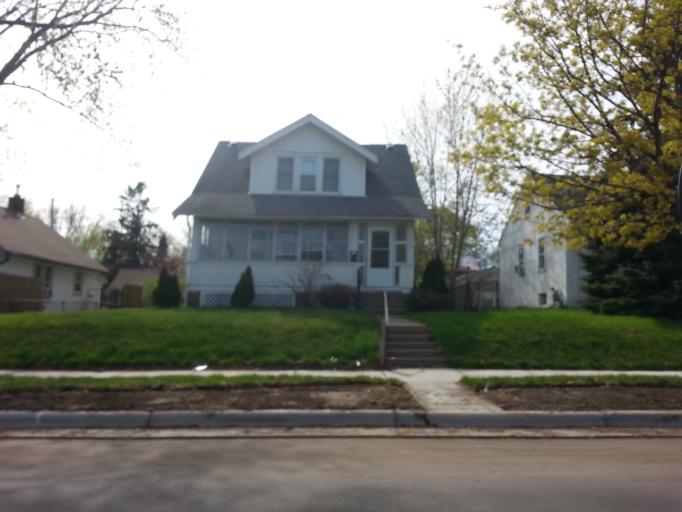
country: US
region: Minnesota
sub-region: Ramsey County
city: Saint Paul
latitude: 44.9816
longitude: -93.0736
